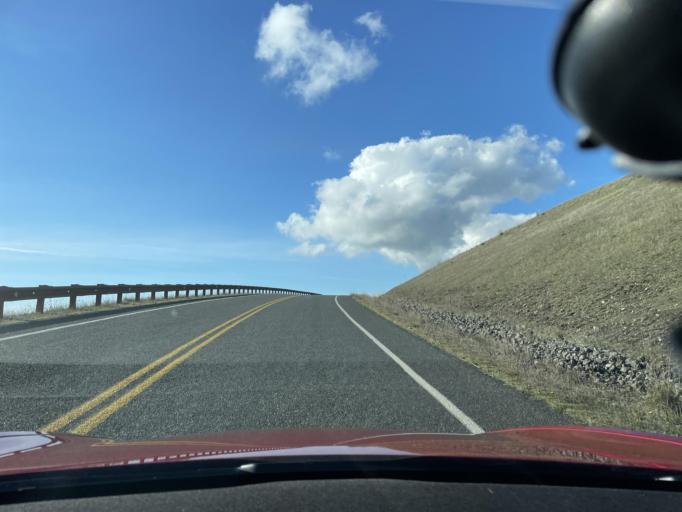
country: US
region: Washington
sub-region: San Juan County
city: Friday Harbor
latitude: 48.4550
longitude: -122.9742
